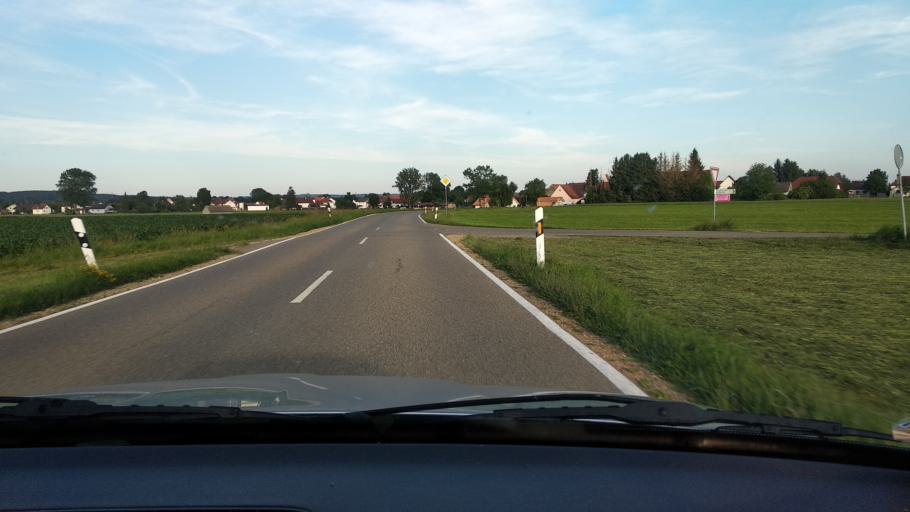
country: DE
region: Baden-Wuerttemberg
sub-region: Tuebingen Region
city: Dettingen an der Iller
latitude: 48.1127
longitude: 10.1045
